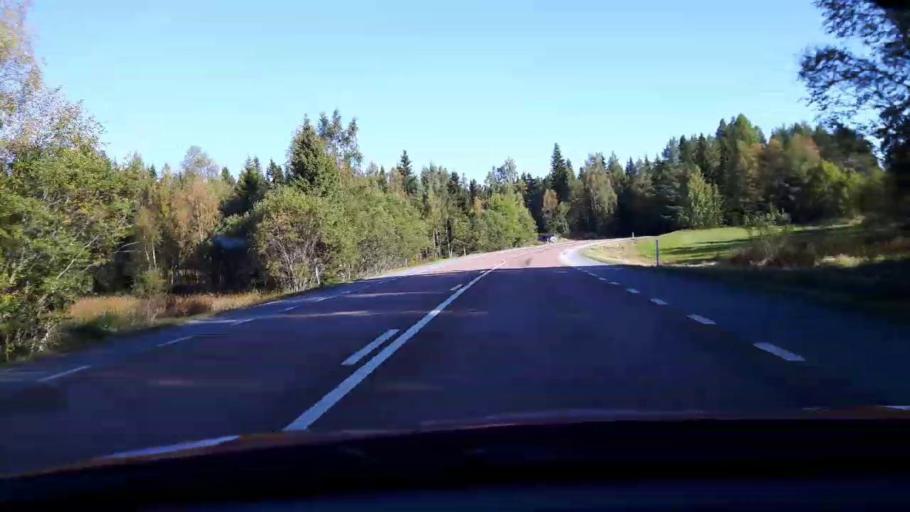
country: SE
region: Jaemtland
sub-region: OEstersunds Kommun
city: Brunflo
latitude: 62.9479
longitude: 15.0837
